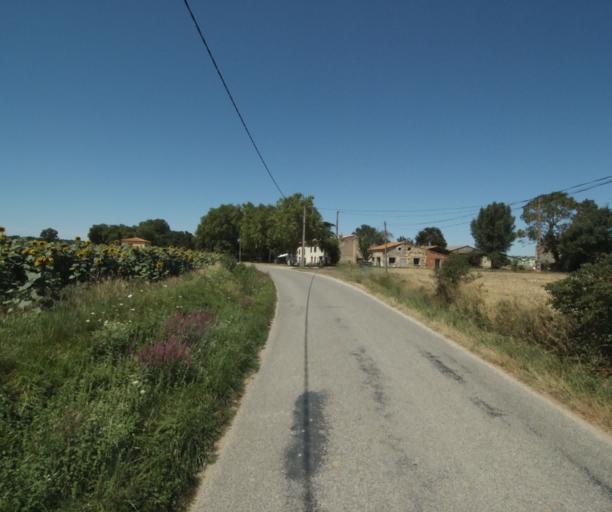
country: FR
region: Midi-Pyrenees
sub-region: Departement de la Haute-Garonne
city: Revel
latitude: 43.4635
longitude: 1.9498
